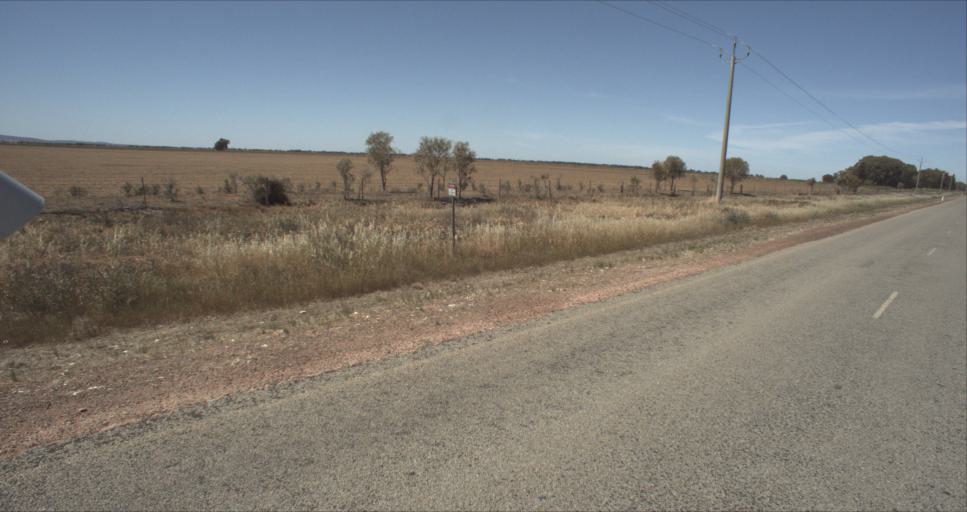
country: AU
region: New South Wales
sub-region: Leeton
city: Leeton
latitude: -34.4597
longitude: 146.2944
